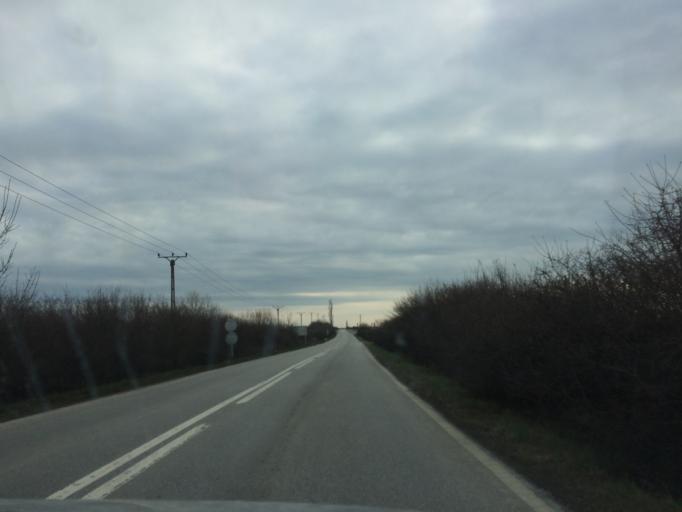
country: RO
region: Timis
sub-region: Oras Deta
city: Deta
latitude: 45.4155
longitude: 21.2284
